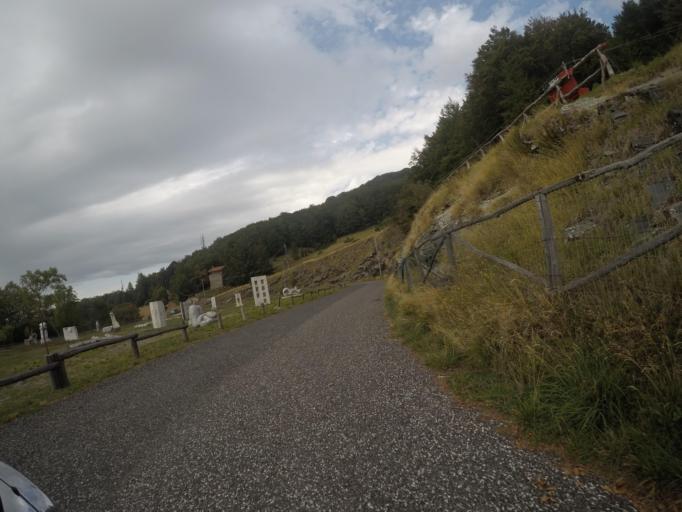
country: IT
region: Tuscany
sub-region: Provincia di Massa-Carrara
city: Carrara
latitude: 44.1211
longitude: 10.1211
